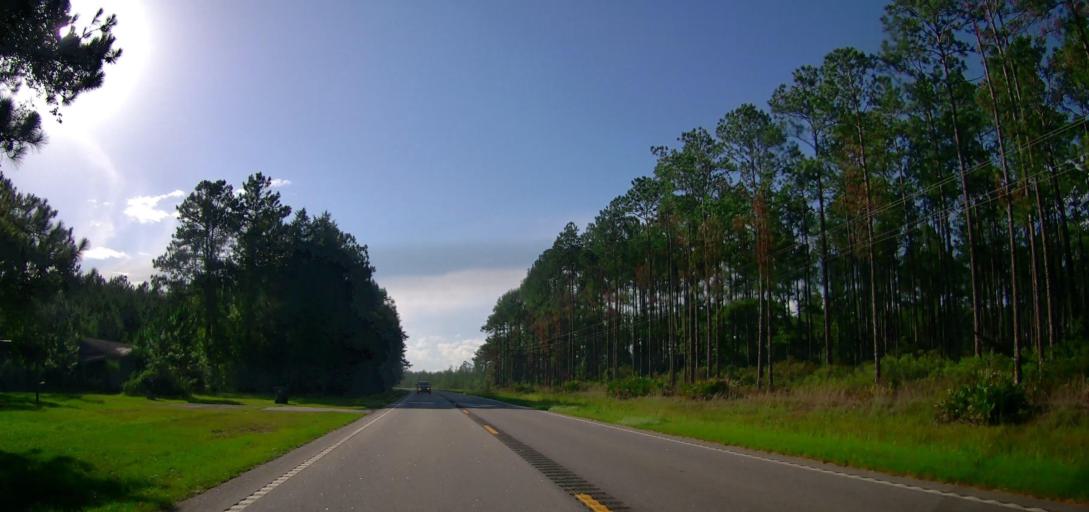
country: US
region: Georgia
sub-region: Coffee County
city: Nicholls
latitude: 31.4520
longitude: -82.7295
